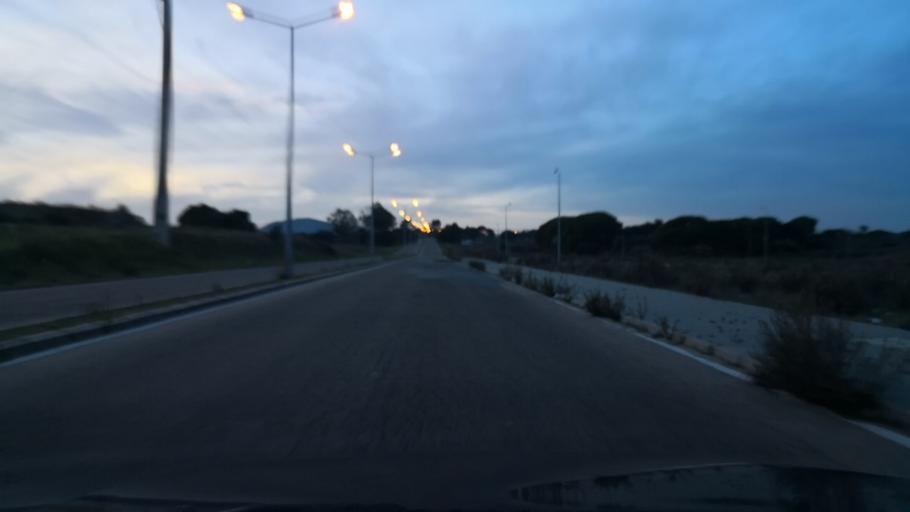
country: PT
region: Setubal
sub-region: Setubal
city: Setubal
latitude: 38.5146
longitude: -8.8546
